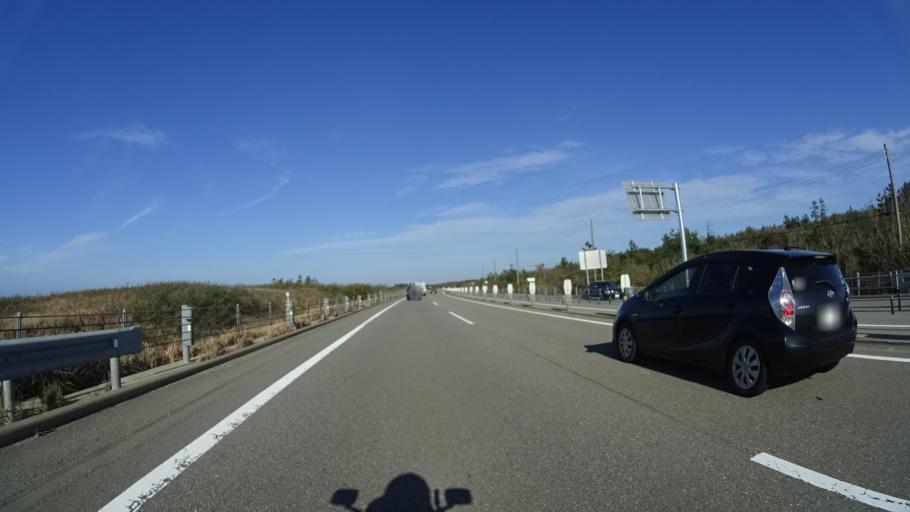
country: JP
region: Ishikawa
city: Kanazawa-shi
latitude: 36.6758
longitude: 136.6529
